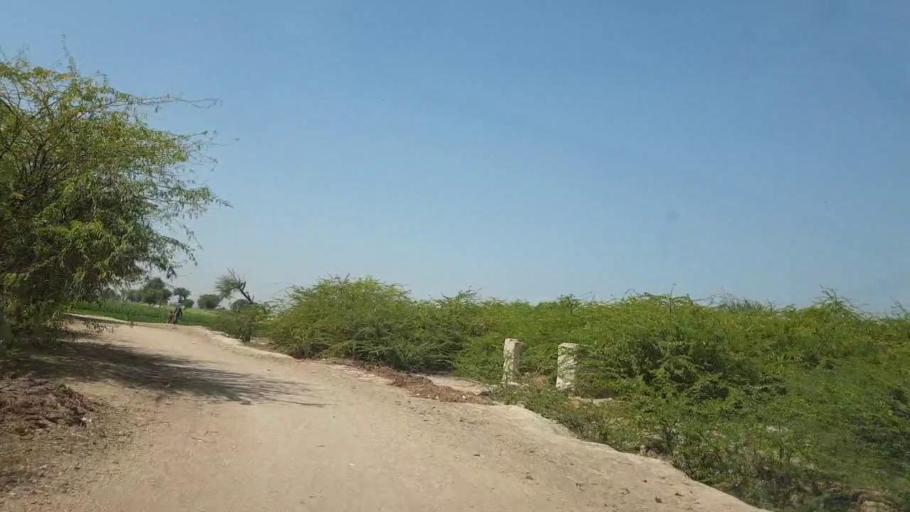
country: PK
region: Sindh
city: Kunri
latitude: 25.1021
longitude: 69.4568
